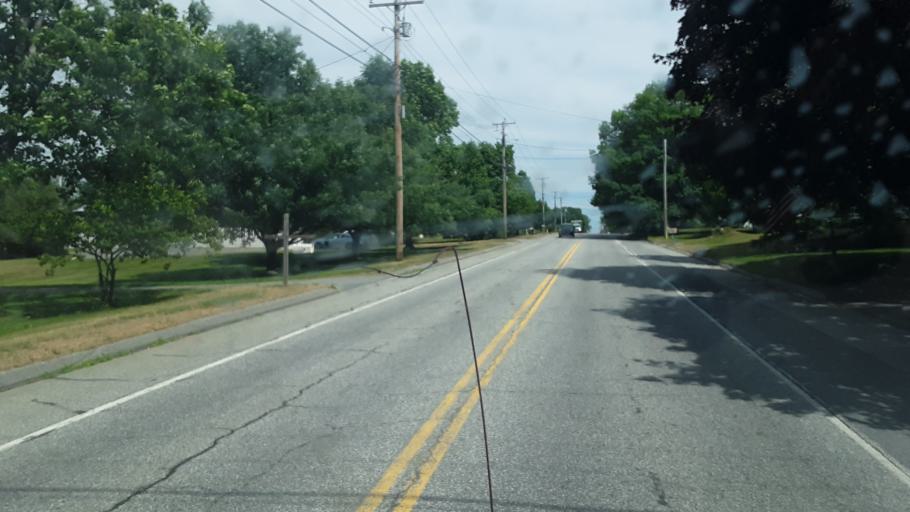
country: US
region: Maine
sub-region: Kennebec County
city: Waterville
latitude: 44.5989
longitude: -69.6472
